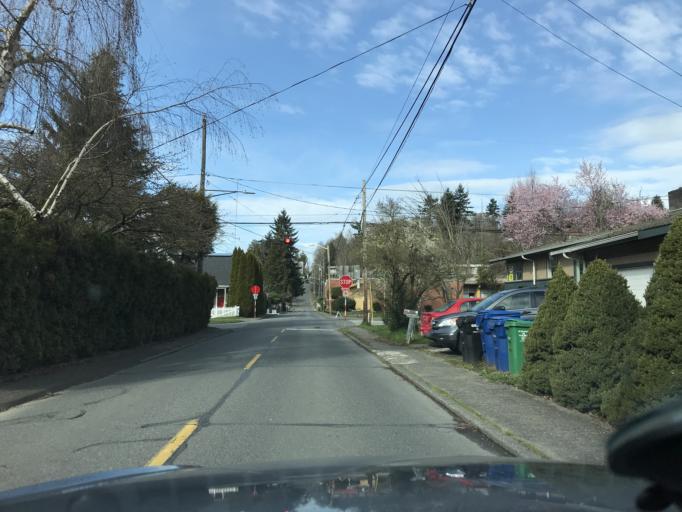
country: US
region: Washington
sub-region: King County
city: Seattle
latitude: 47.6221
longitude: -122.2912
